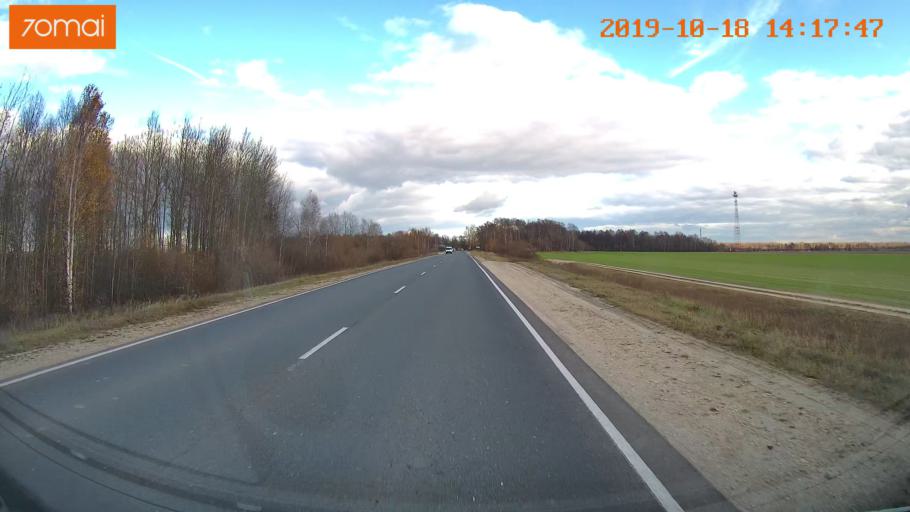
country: RU
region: Rjazan
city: Tuma
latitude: 55.1397
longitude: 40.3803
